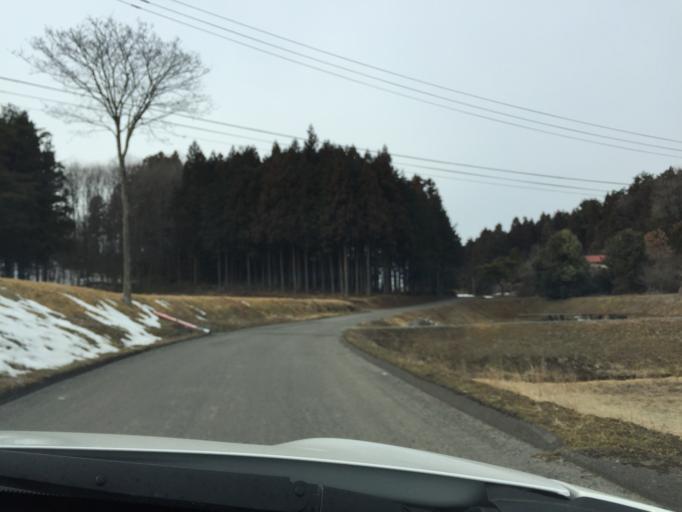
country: JP
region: Fukushima
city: Ishikawa
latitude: 37.1986
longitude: 140.5688
